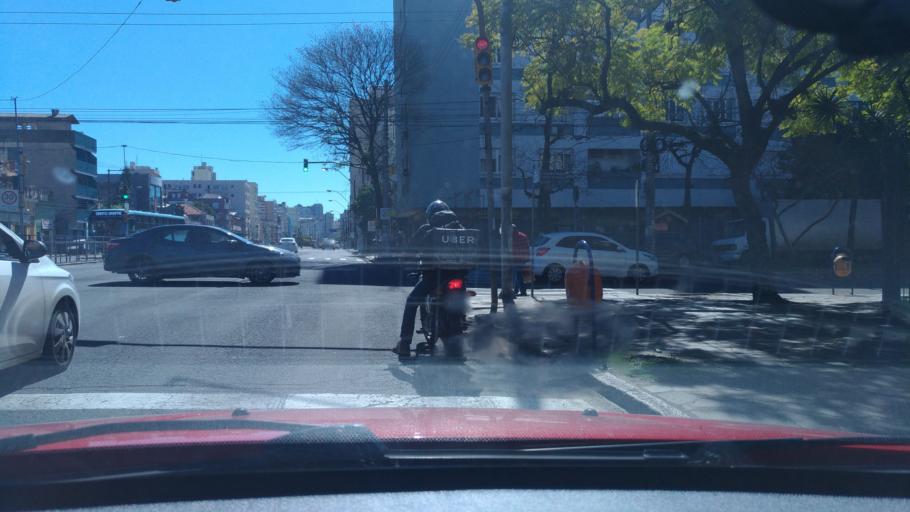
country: BR
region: Rio Grande do Sul
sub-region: Porto Alegre
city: Porto Alegre
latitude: -30.0435
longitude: -51.2144
